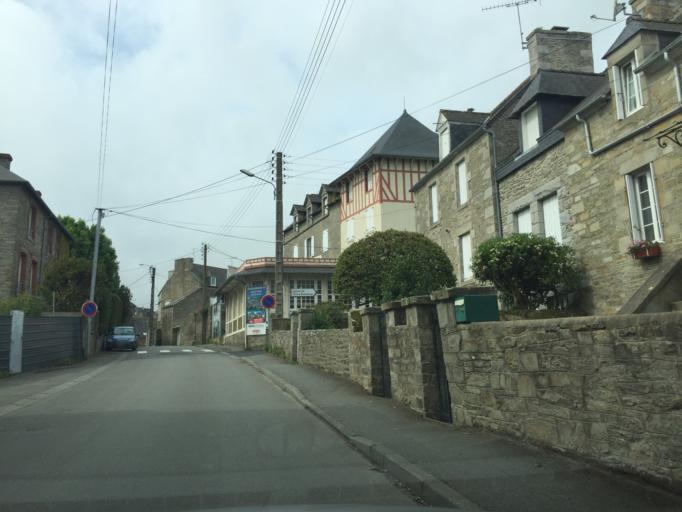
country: FR
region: Brittany
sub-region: Departement des Cotes-d'Armor
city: Saint-Cast-le-Guildo
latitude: 48.6395
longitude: -2.2561
